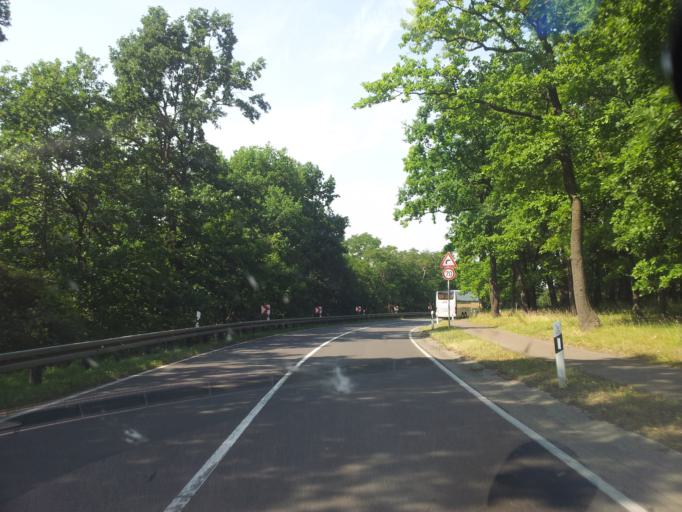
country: DE
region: Saxony
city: Stauchitz
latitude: 51.2471
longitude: 13.2175
